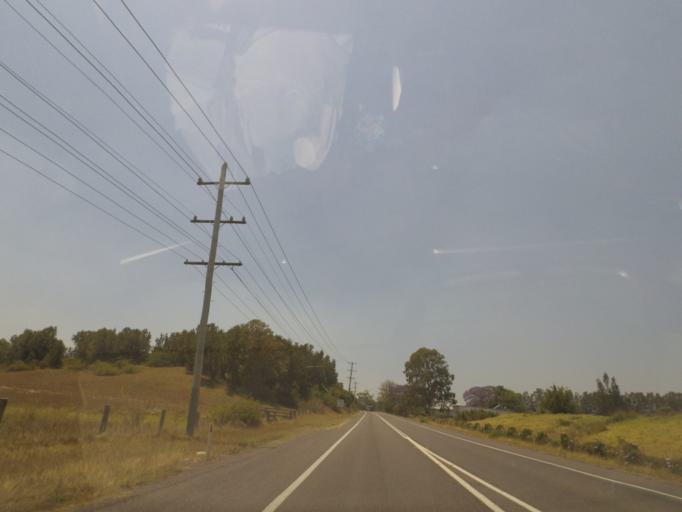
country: AU
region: New South Wales
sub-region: Port Stephens Shire
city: Medowie
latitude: -32.8070
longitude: 151.8685
